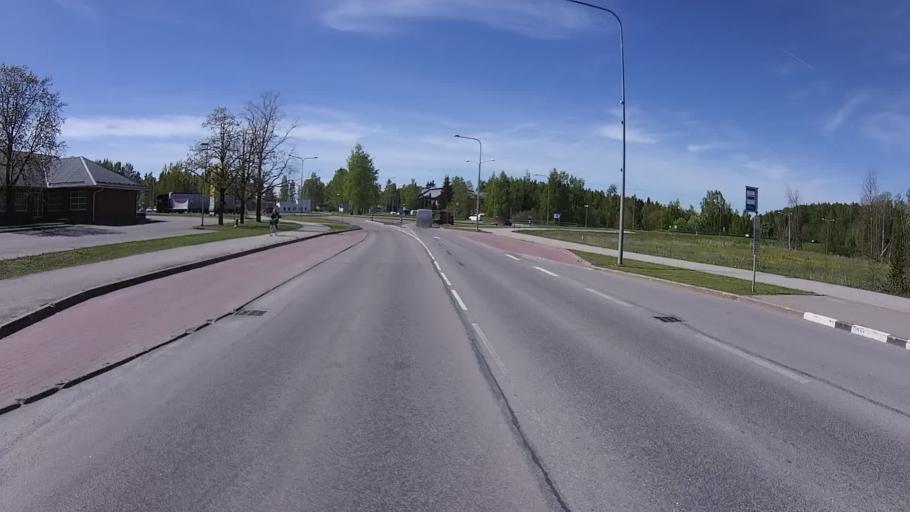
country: EE
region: Polvamaa
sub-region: Polva linn
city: Polva
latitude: 58.0678
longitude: 27.0753
